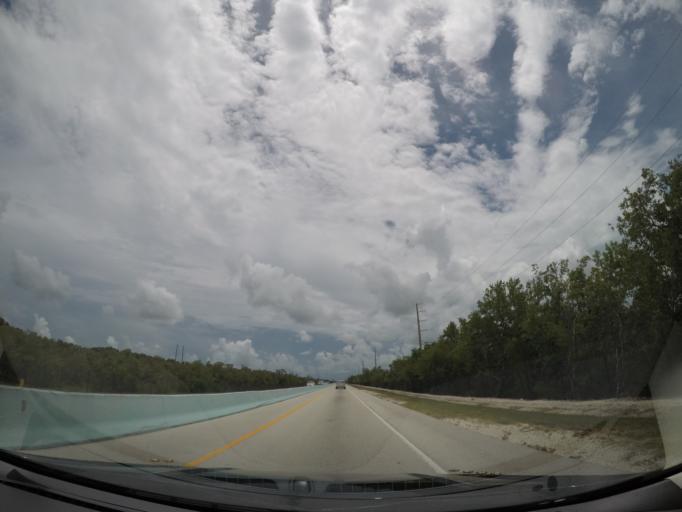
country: US
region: Florida
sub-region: Monroe County
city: North Key Largo
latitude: 25.2214
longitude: -80.4295
